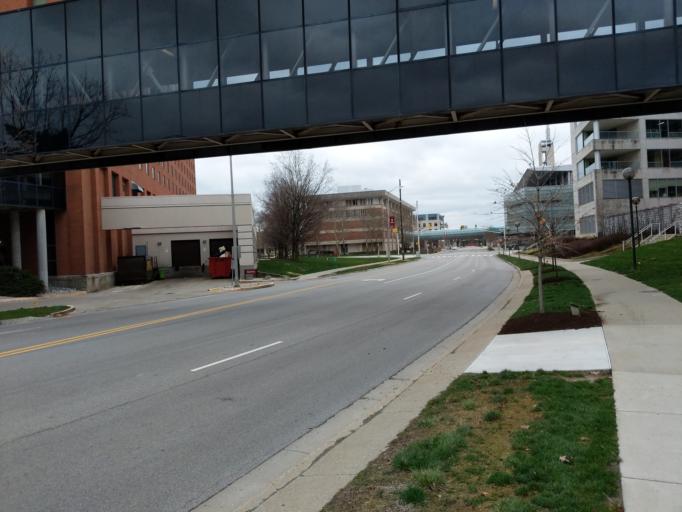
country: US
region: Indiana
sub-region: Marion County
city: Indianapolis
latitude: 39.7757
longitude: -86.1755
